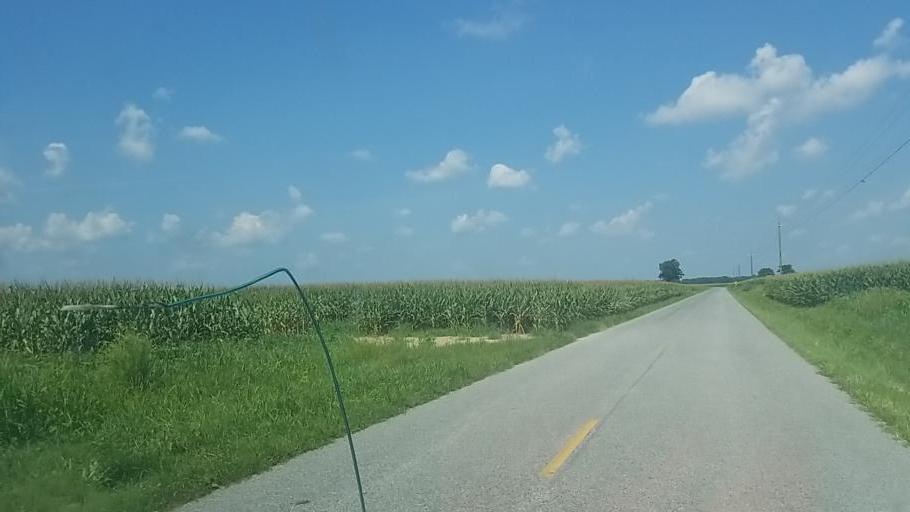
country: US
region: Maryland
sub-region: Worcester County
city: Berlin
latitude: 38.2911
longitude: -75.2447
